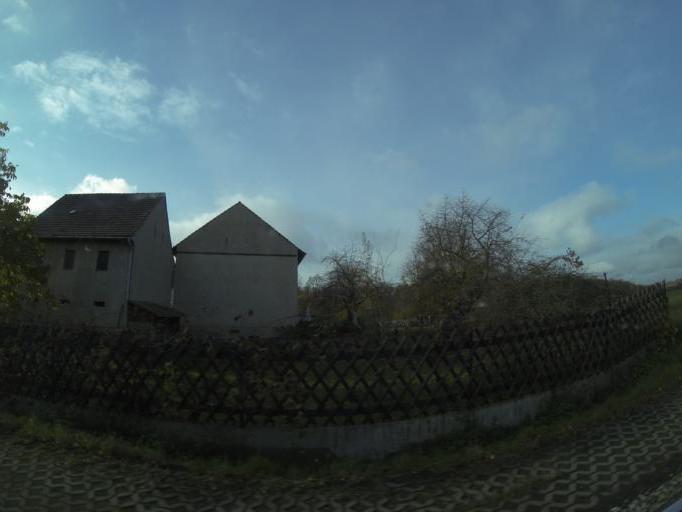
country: DE
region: Thuringia
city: Gossnitz
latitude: 50.9121
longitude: 12.4427
